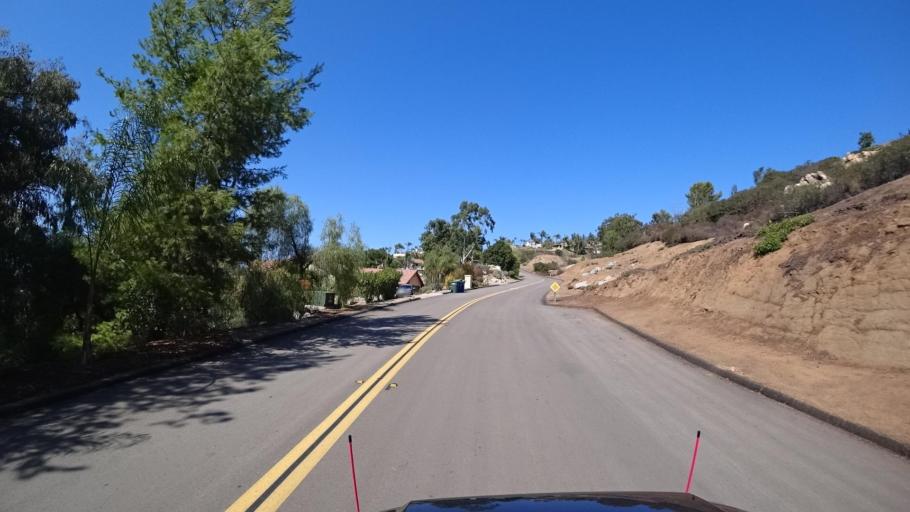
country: US
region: California
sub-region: San Diego County
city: Granite Hills
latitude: 32.8012
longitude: -116.8949
